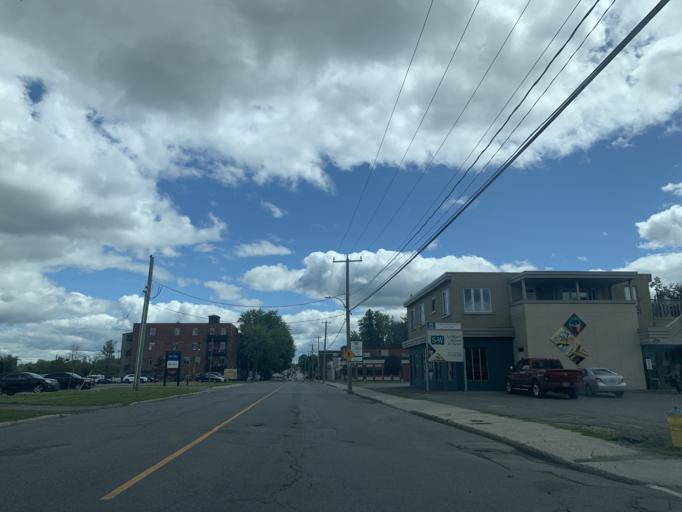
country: CA
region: Ontario
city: Hawkesbury
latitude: 45.6104
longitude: -74.6190
